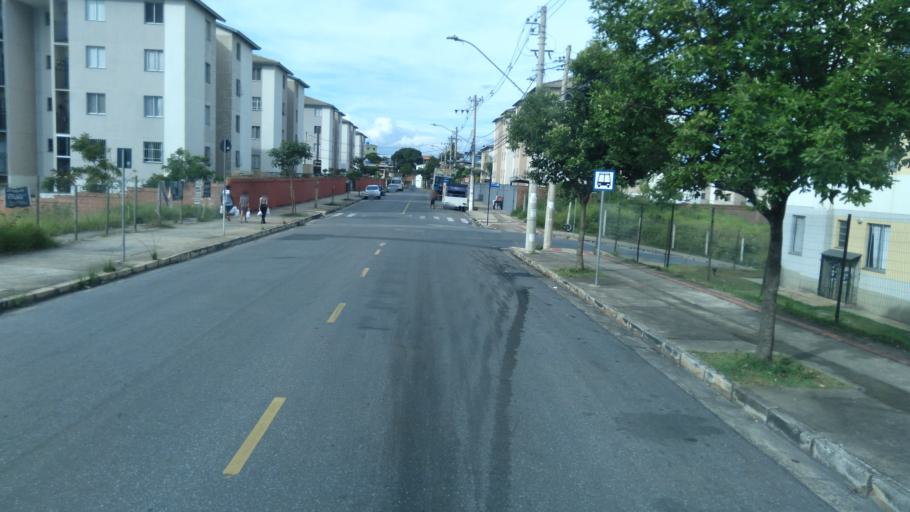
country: BR
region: Minas Gerais
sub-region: Santa Luzia
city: Santa Luzia
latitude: -19.8415
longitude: -43.8897
